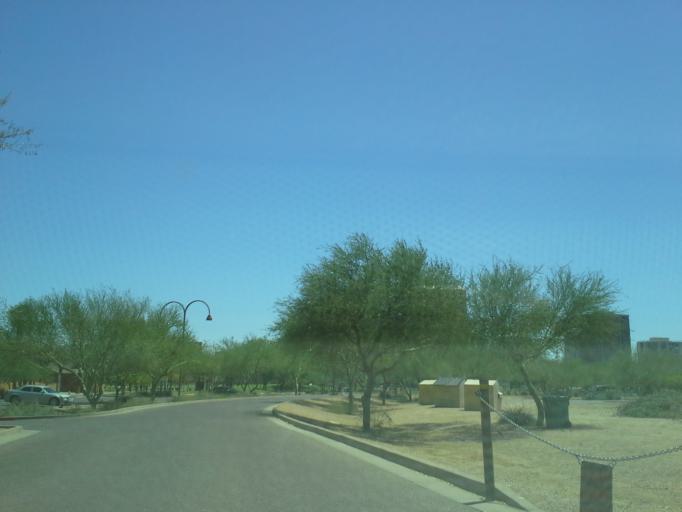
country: US
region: Arizona
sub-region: Maricopa County
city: Phoenix
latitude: 33.4993
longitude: -112.0715
